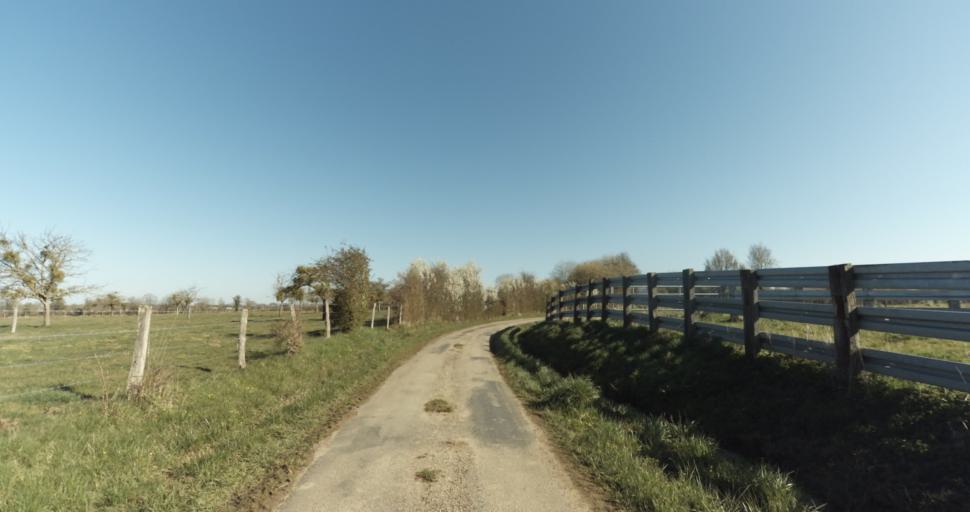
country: FR
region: Lower Normandy
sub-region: Departement du Calvados
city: Saint-Pierre-sur-Dives
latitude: 48.9589
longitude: 0.0181
